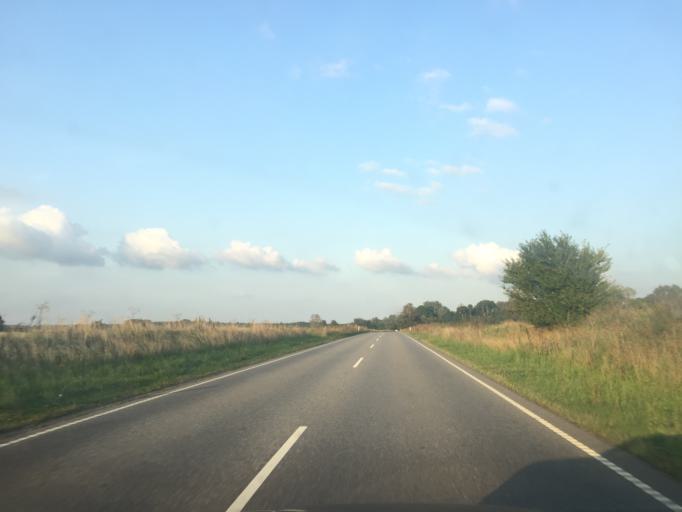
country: DK
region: Zealand
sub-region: Holbaek Kommune
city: Tollose
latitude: 55.5554
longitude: 11.7604
